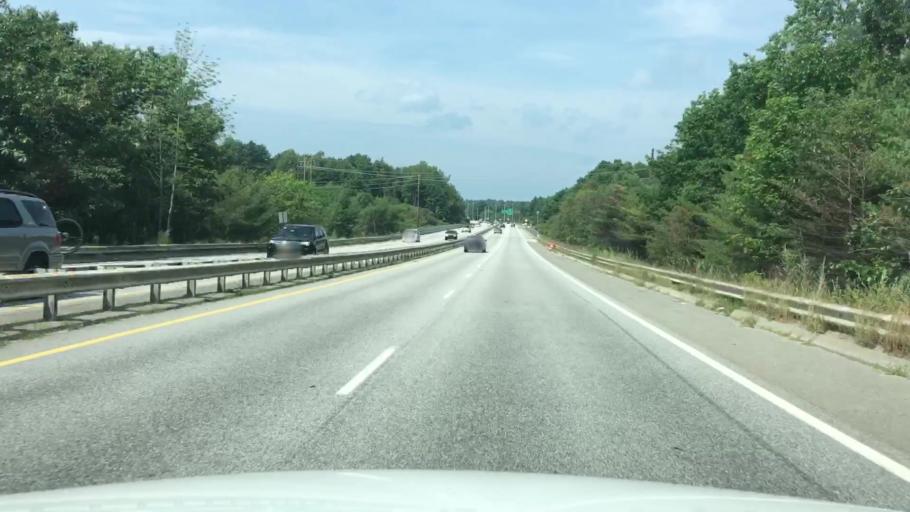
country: US
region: Maine
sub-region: Androscoggin County
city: Lewiston
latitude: 44.1155
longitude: -70.2142
